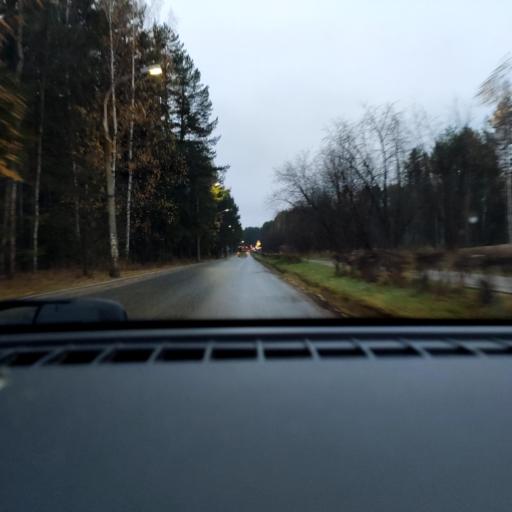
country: RU
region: Perm
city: Perm
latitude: 58.0532
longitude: 56.2144
